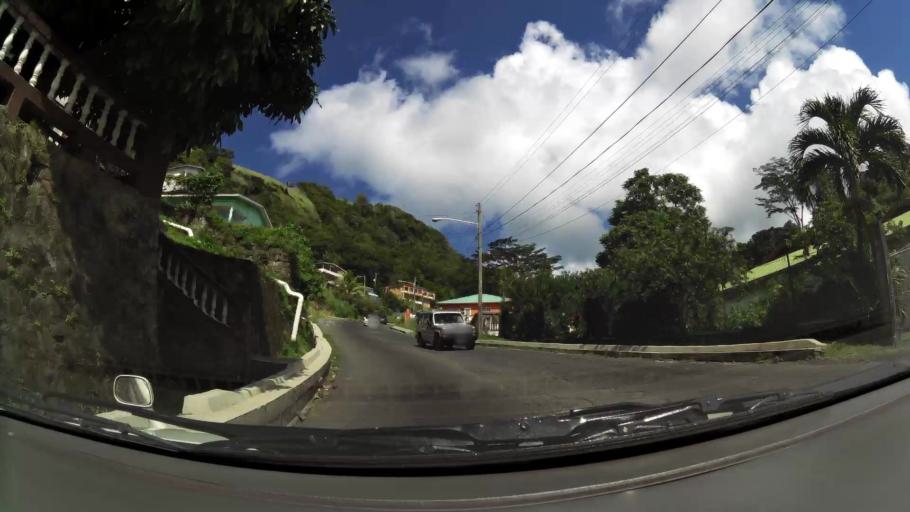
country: VC
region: Saint George
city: Kingstown
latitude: 13.1689
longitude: -61.2283
